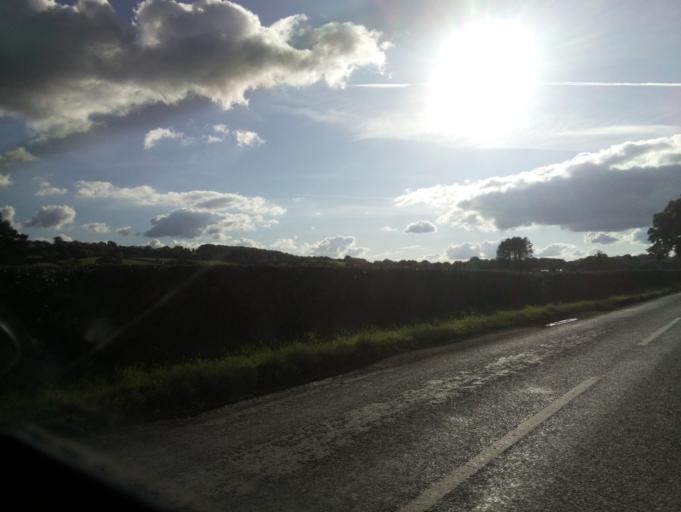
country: GB
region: England
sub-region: Herefordshire
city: Clifford
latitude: 52.1154
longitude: -3.0889
